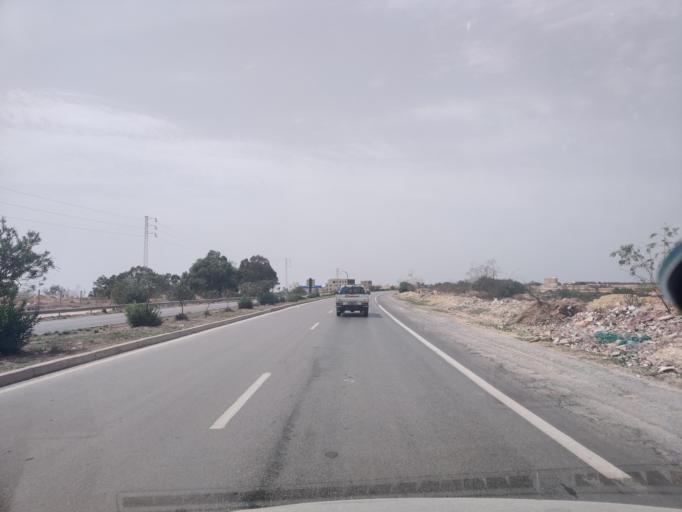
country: TN
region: Susah
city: Akouda
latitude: 35.8357
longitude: 10.5481
